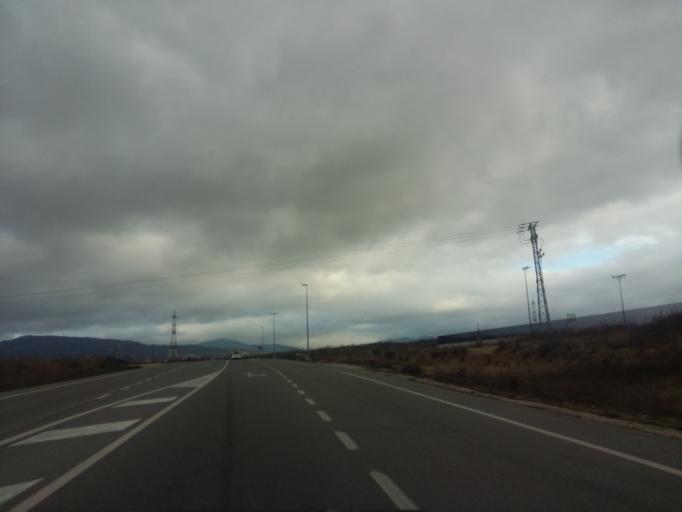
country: ES
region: Navarre
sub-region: Provincia de Navarra
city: Iturrama
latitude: 42.7890
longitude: -1.6534
